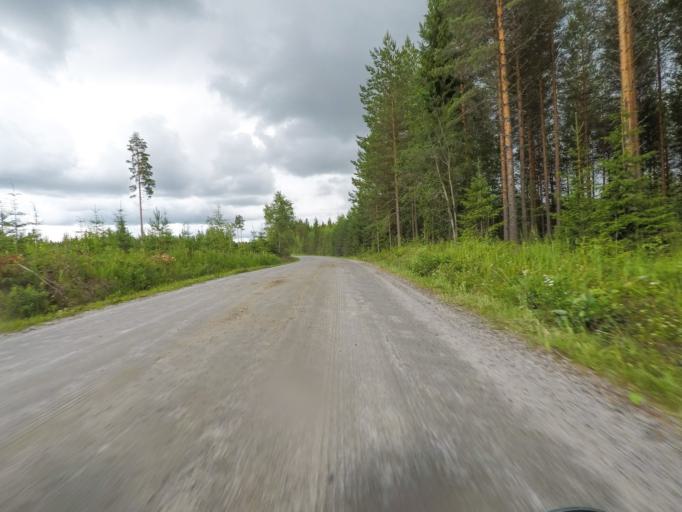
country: FI
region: Central Finland
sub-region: Jyvaeskylae
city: Hankasalmi
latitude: 62.3960
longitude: 26.5956
